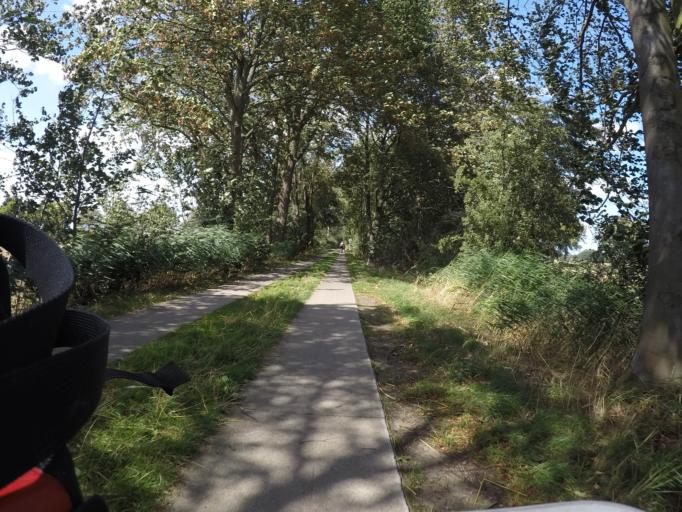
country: DE
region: Lower Saxony
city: Stelle
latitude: 53.4587
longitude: 10.1111
